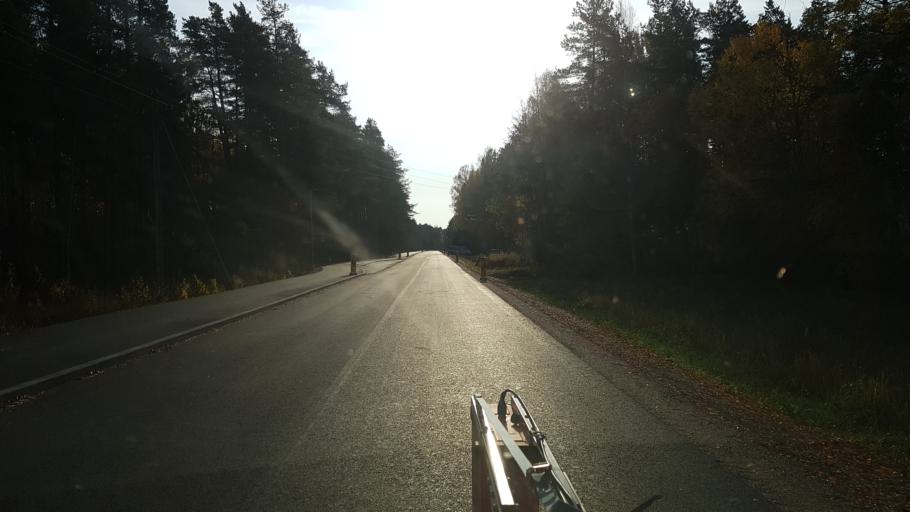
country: EE
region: Paernumaa
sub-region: Paikuse vald
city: Paikuse
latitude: 58.3582
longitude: 24.6126
